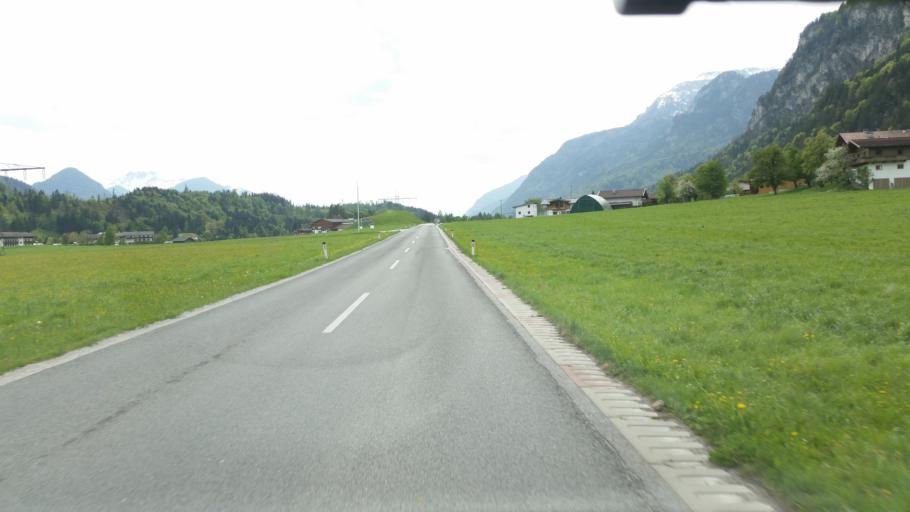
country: AT
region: Tyrol
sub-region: Politischer Bezirk Kufstein
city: Radfeld
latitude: 47.4671
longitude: 11.9114
